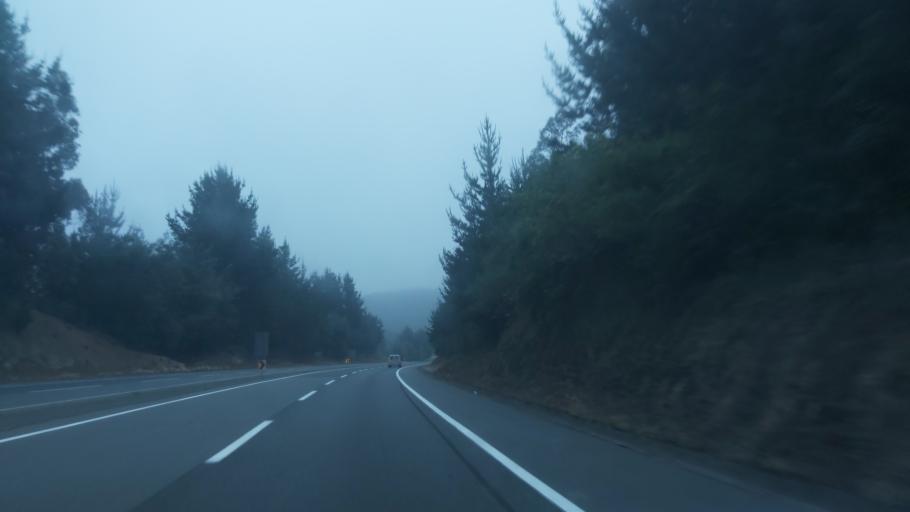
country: CL
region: Biobio
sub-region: Provincia de Concepcion
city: Penco
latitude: -36.7383
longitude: -72.8945
